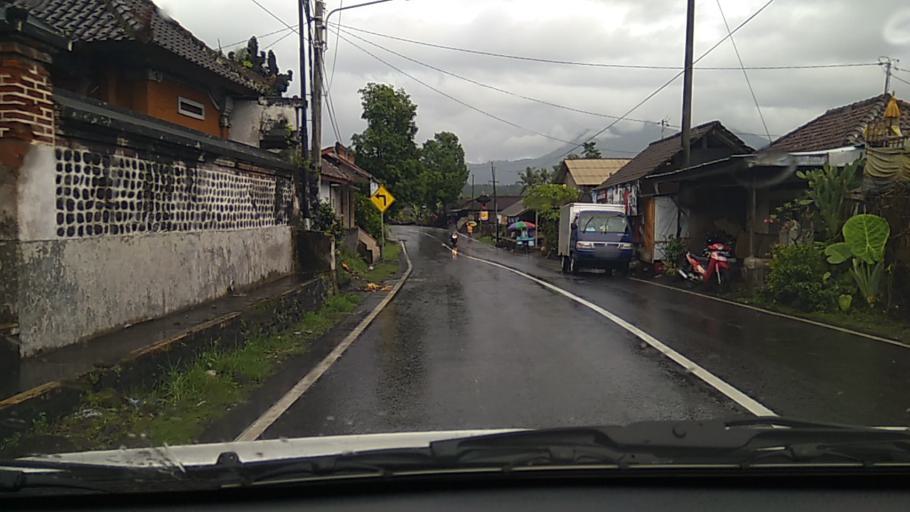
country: ID
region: Bali
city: Banjar Ababi
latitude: -8.4211
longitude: 115.5915
